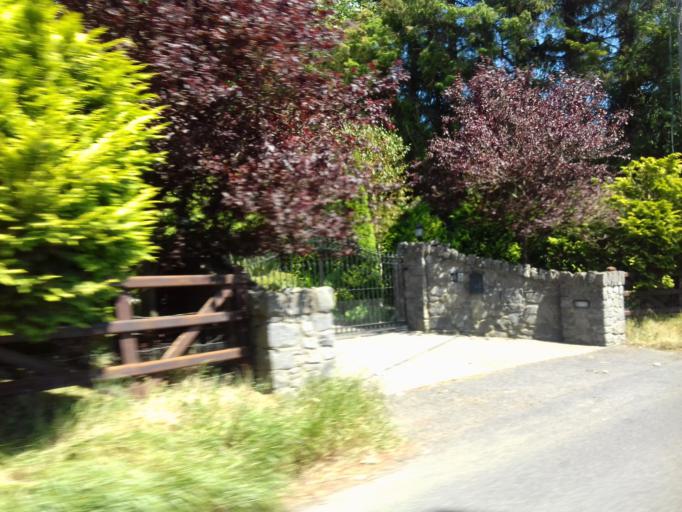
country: IE
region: Leinster
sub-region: An Mhi
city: Ashbourne
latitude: 53.5267
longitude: -6.3220
